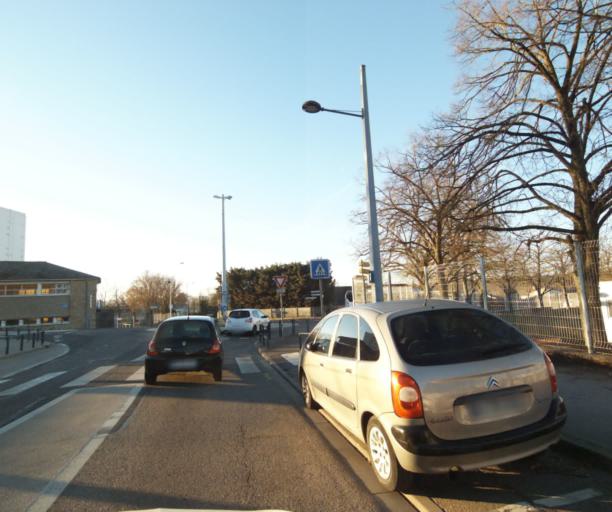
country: FR
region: Lorraine
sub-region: Departement de Meurthe-et-Moselle
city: Laxou
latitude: 48.6910
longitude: 6.1385
